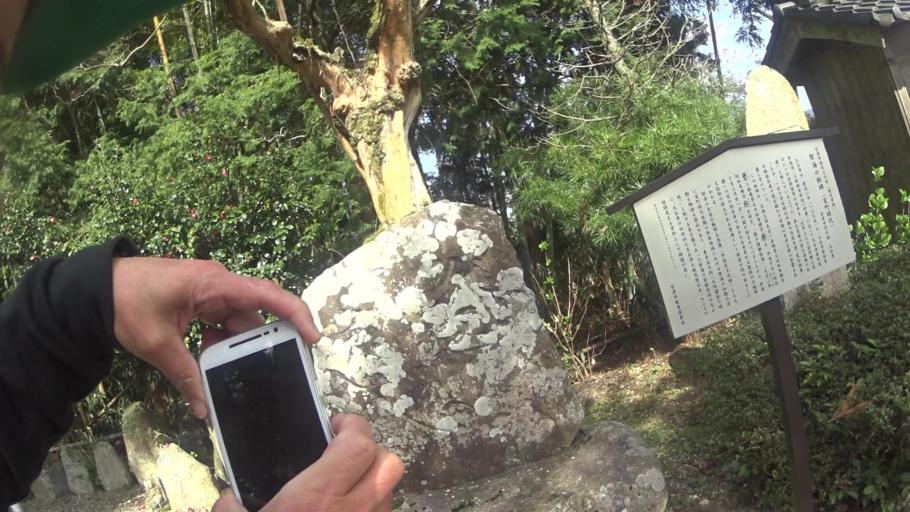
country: JP
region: Kyoto
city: Miyazu
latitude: 35.5833
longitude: 135.1953
